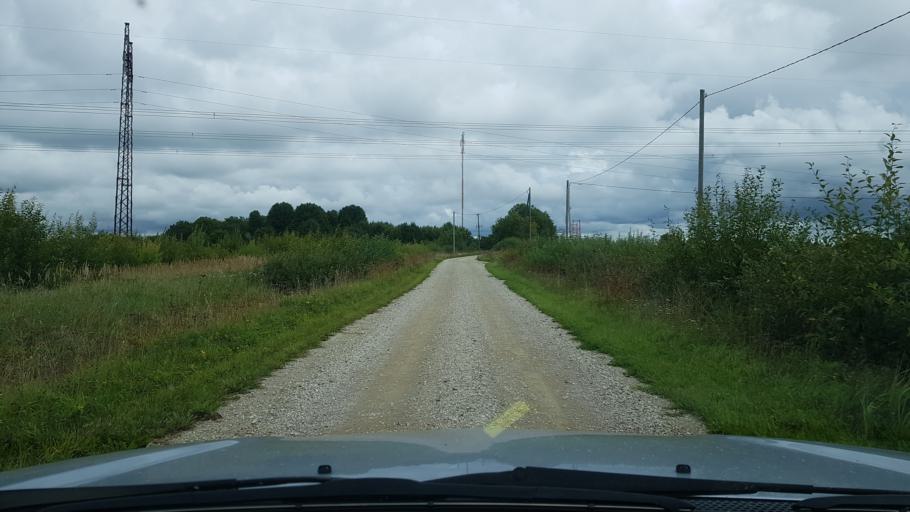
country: EE
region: Harju
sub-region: Rae vald
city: Vaida
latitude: 59.2778
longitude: 24.9702
